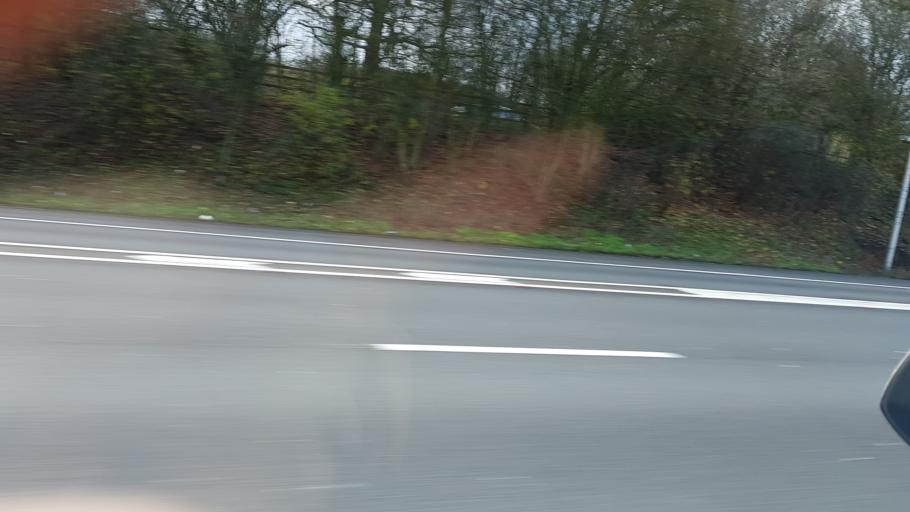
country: GB
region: England
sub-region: Hertfordshire
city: Abbots Langley
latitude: 51.7202
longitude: -0.3873
